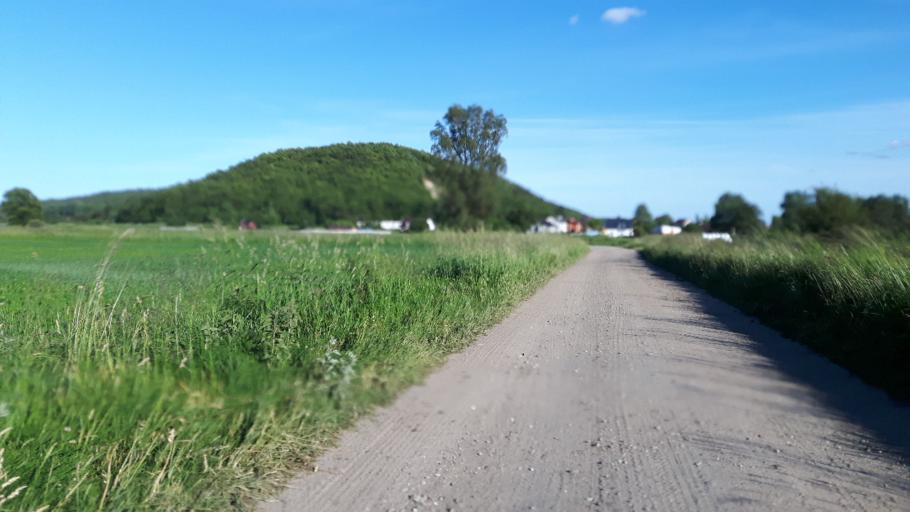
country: PL
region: Pomeranian Voivodeship
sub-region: Powiat wejherowski
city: Rumia
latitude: 54.6070
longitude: 18.4179
